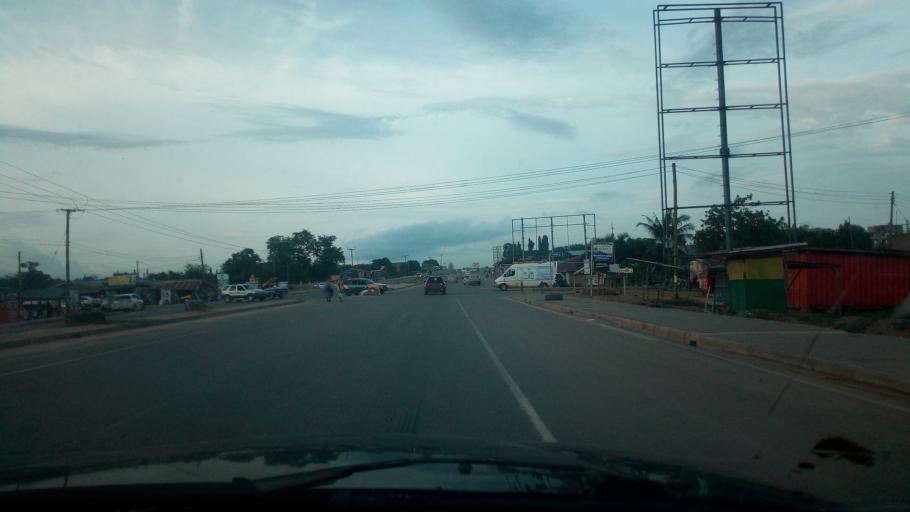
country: GH
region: Western
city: Takoradi
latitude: 4.9176
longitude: -1.7902
